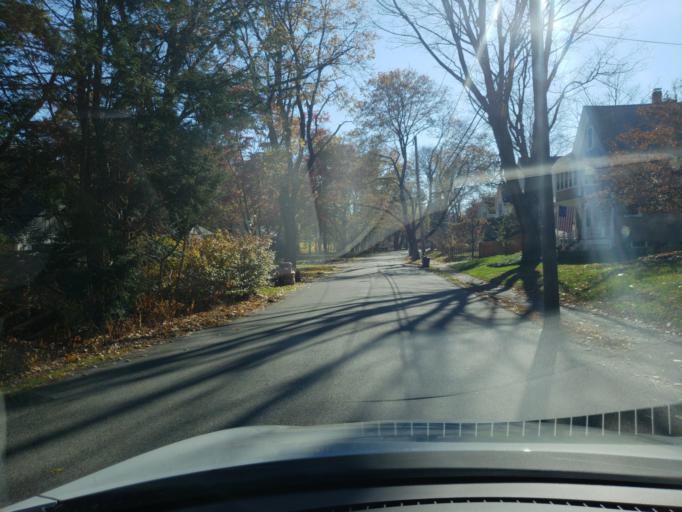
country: US
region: Massachusetts
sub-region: Essex County
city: Andover
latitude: 42.6614
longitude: -71.1310
